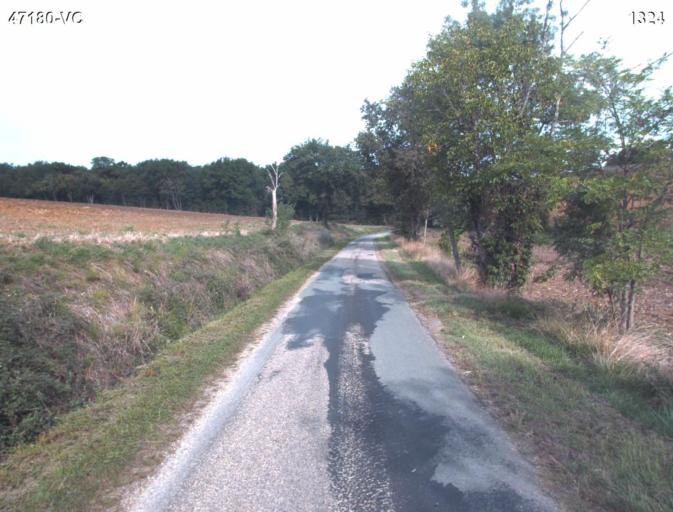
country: FR
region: Aquitaine
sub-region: Departement du Lot-et-Garonne
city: Sainte-Colombe-en-Bruilhois
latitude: 44.1786
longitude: 0.4412
